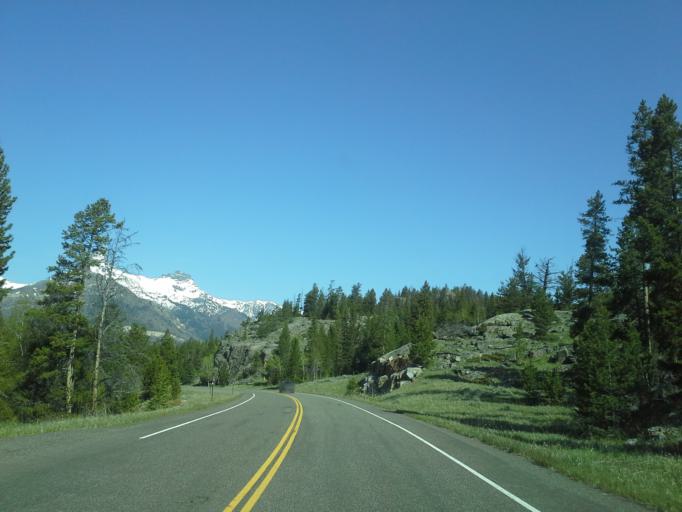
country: US
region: Montana
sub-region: Carbon County
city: Red Lodge
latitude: 44.9480
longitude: -109.7855
